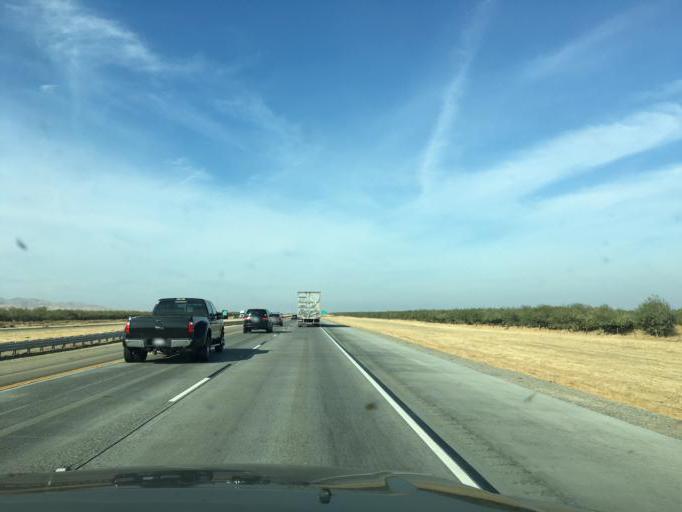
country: US
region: California
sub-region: Fresno County
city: Firebaugh
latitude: 36.6669
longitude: -120.6435
